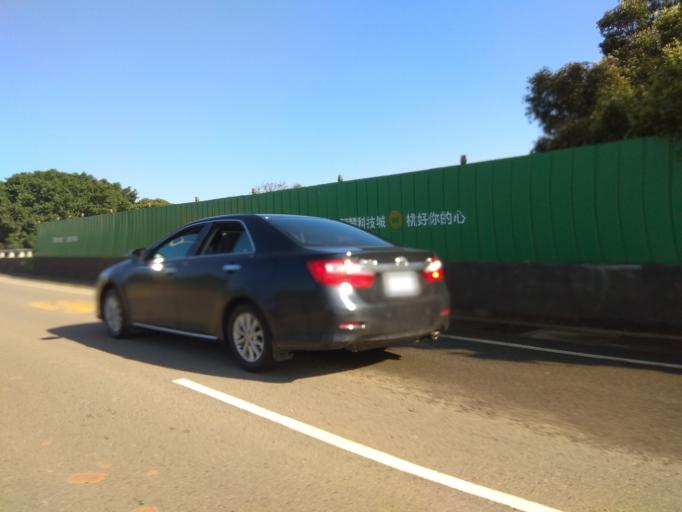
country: TW
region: Taiwan
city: Taoyuan City
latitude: 25.0406
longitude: 121.1331
